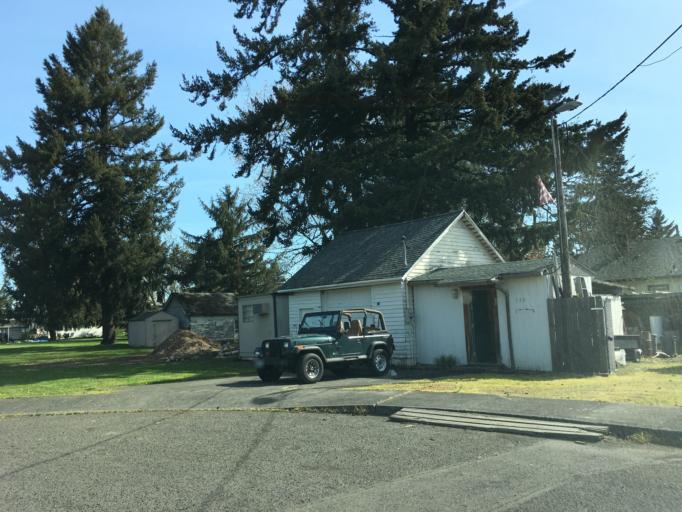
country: US
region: Oregon
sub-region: Multnomah County
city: Lents
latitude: 45.5238
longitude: -122.5692
